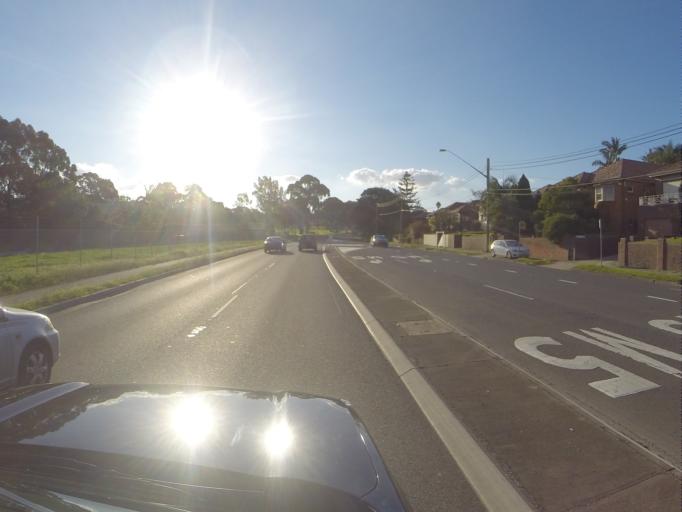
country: AU
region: New South Wales
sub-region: Rockdale
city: Bexley North
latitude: -33.9353
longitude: 151.1111
